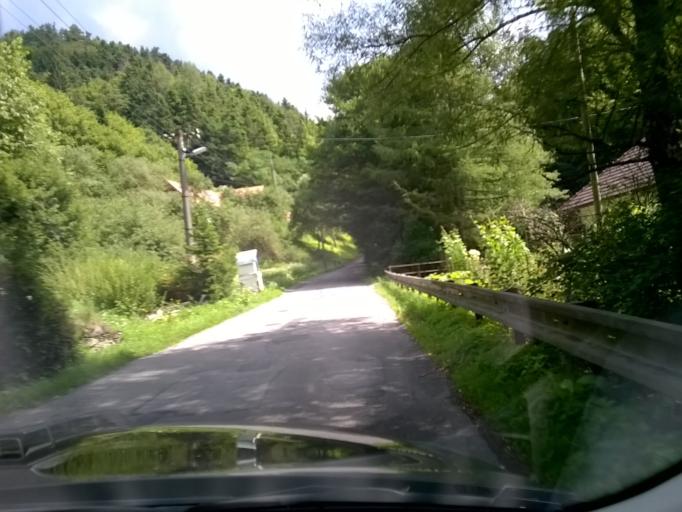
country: SK
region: Banskobystricky
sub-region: Okres Banska Bystrica
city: Banska Stiavnica
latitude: 48.4645
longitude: 18.8294
